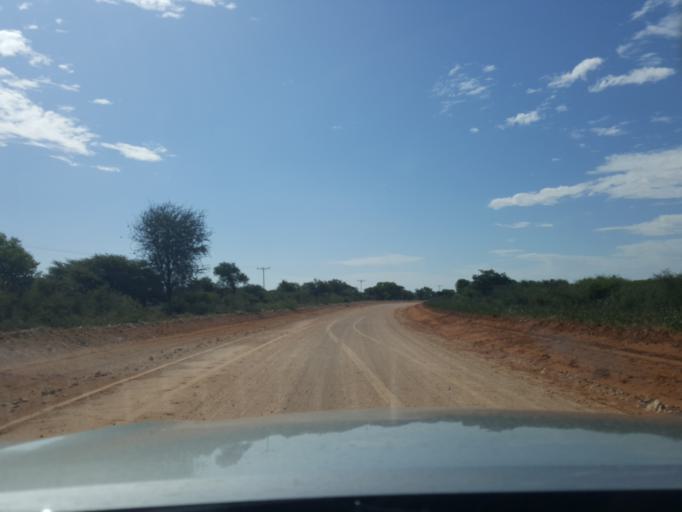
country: BW
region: Kweneng
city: Khudumelapye
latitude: -23.7779
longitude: 24.7703
